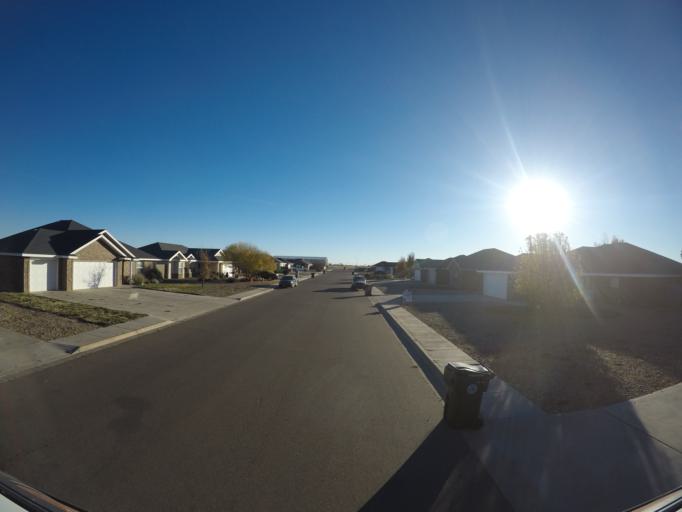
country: US
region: New Mexico
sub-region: Curry County
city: Clovis
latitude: 34.4081
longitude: -103.1704
